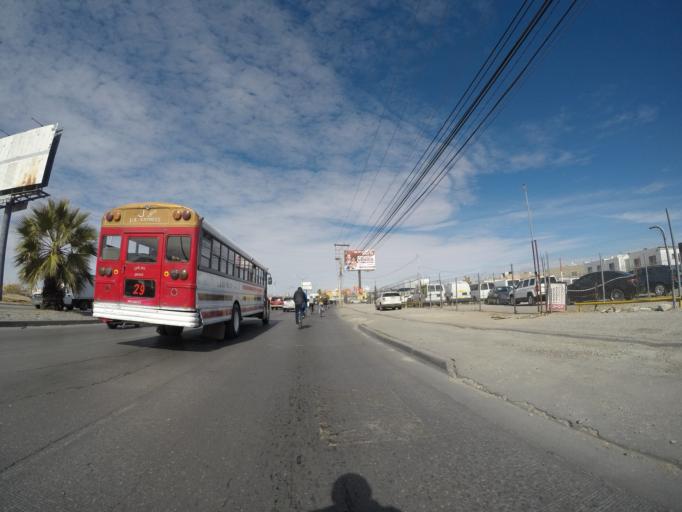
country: MX
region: Chihuahua
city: Ciudad Juarez
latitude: 31.6774
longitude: -106.4085
